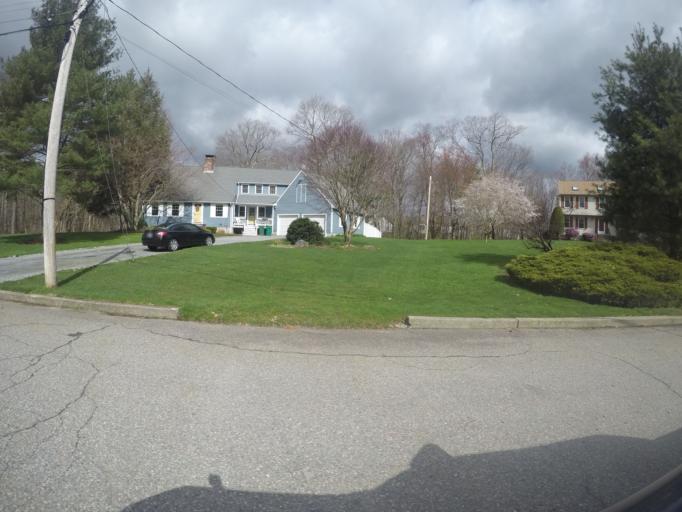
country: US
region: Massachusetts
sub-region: Bristol County
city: Easton
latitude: 42.0359
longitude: -71.1285
